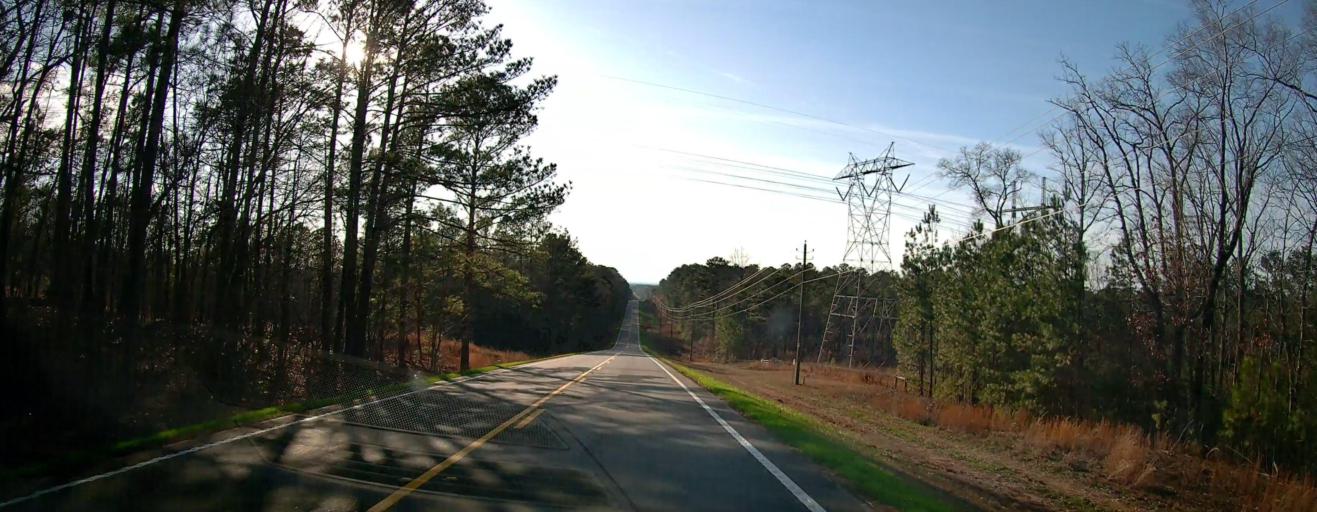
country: US
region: Georgia
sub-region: Harris County
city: Hamilton
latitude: 32.7471
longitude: -84.9844
